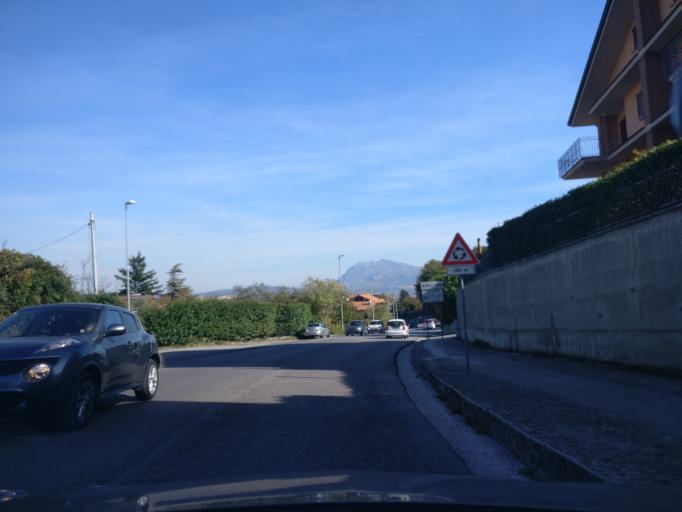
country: IT
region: Campania
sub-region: Provincia di Avellino
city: Torelli-Torrette
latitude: 40.9131
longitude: 14.7629
